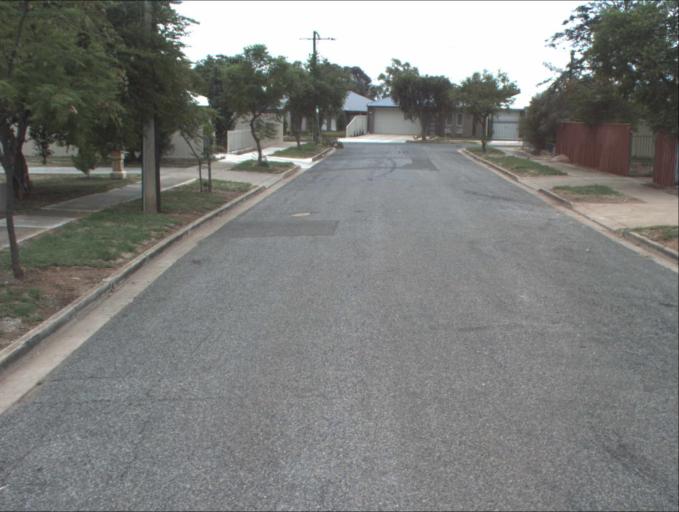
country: AU
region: South Australia
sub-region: Port Adelaide Enfield
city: Enfield
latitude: -34.8549
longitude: 138.6207
